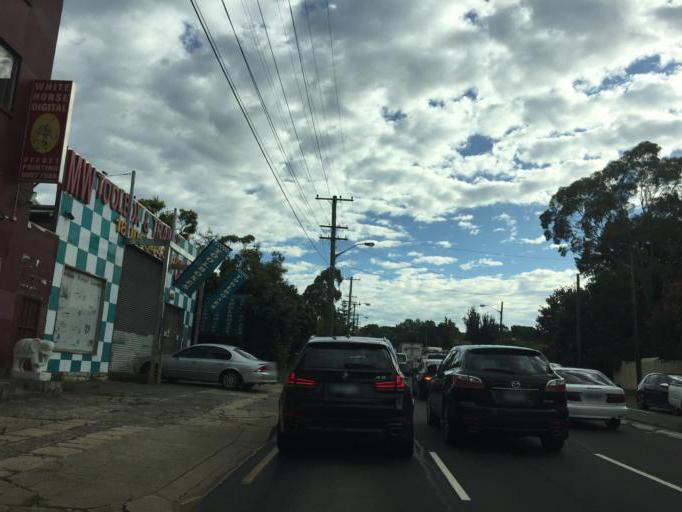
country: AU
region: New South Wales
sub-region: Canada Bay
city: Rhodes
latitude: -33.8208
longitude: 151.0982
